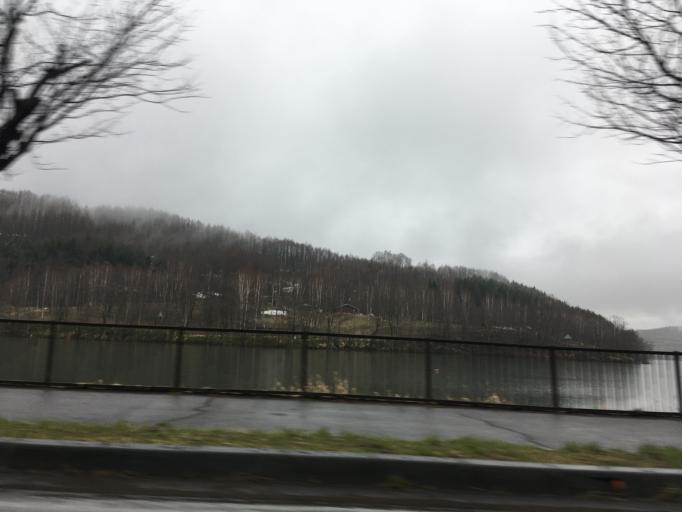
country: JP
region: Hokkaido
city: Nayoro
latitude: 44.0954
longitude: 142.4371
